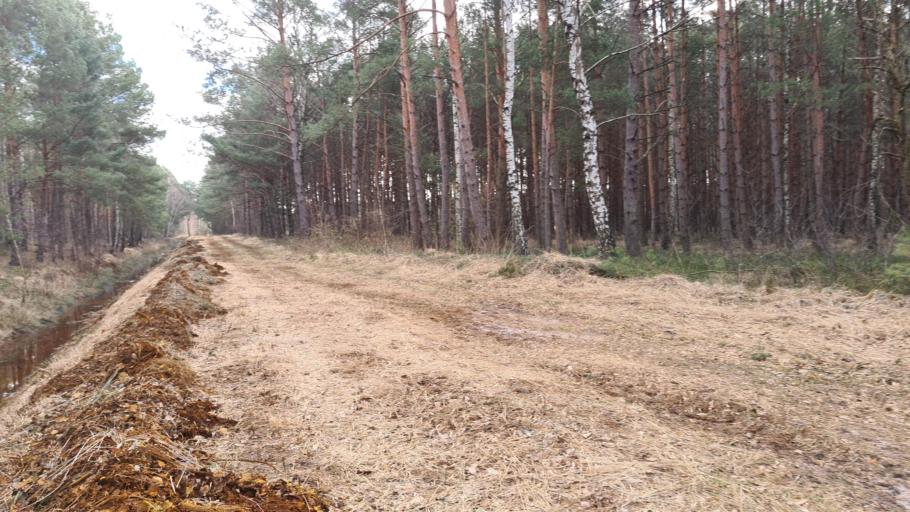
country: DE
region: Brandenburg
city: Finsterwalde
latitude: 51.5546
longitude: 13.6591
